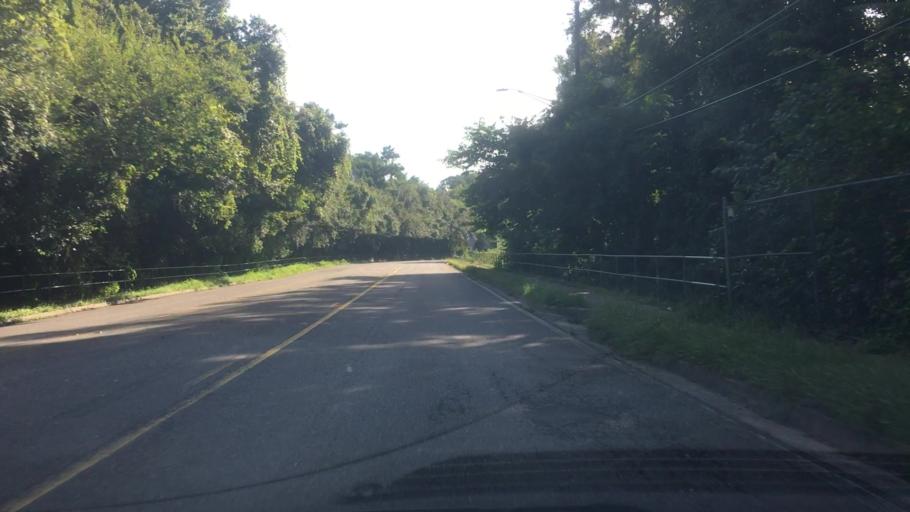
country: US
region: Florida
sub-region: Duval County
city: Jacksonville
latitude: 30.2916
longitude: -81.6148
